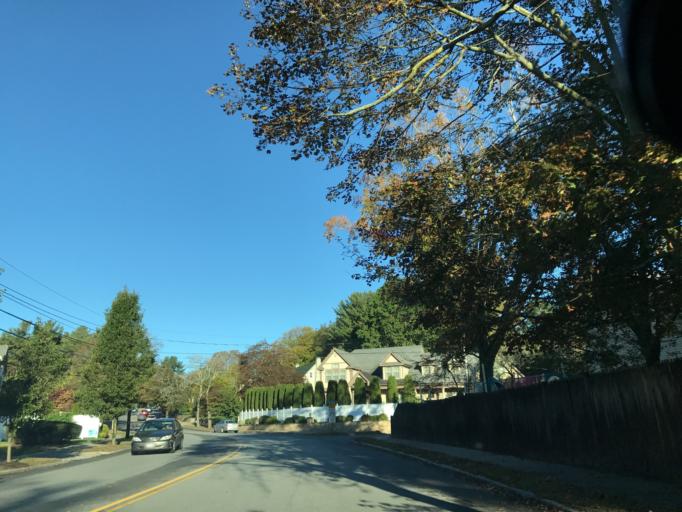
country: US
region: Massachusetts
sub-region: Middlesex County
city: Newton
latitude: 42.2974
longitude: -71.1829
